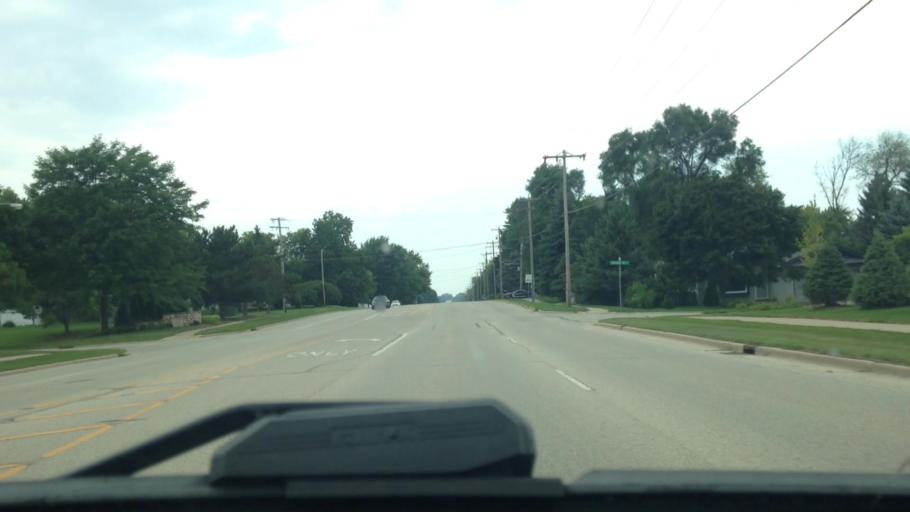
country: US
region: Wisconsin
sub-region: Waukesha County
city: Menomonee Falls
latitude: 43.1583
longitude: -88.1041
